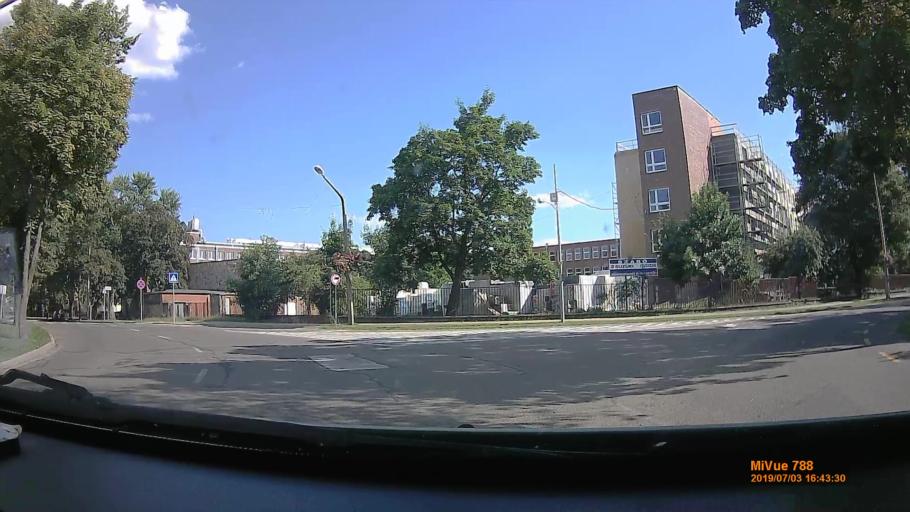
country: HU
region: Borsod-Abauj-Zemplen
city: Kazincbarcika
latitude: 48.2482
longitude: 20.6163
